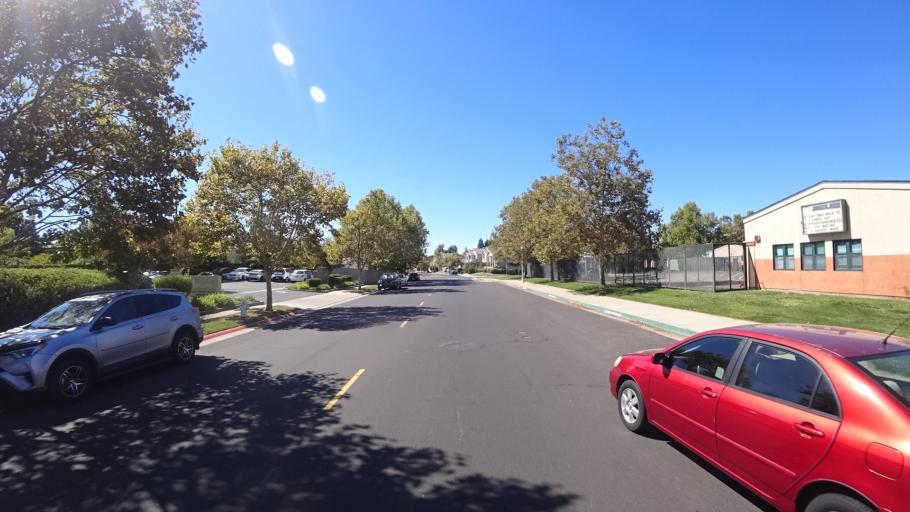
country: US
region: California
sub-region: Sacramento County
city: Laguna
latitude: 38.4176
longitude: -121.4701
